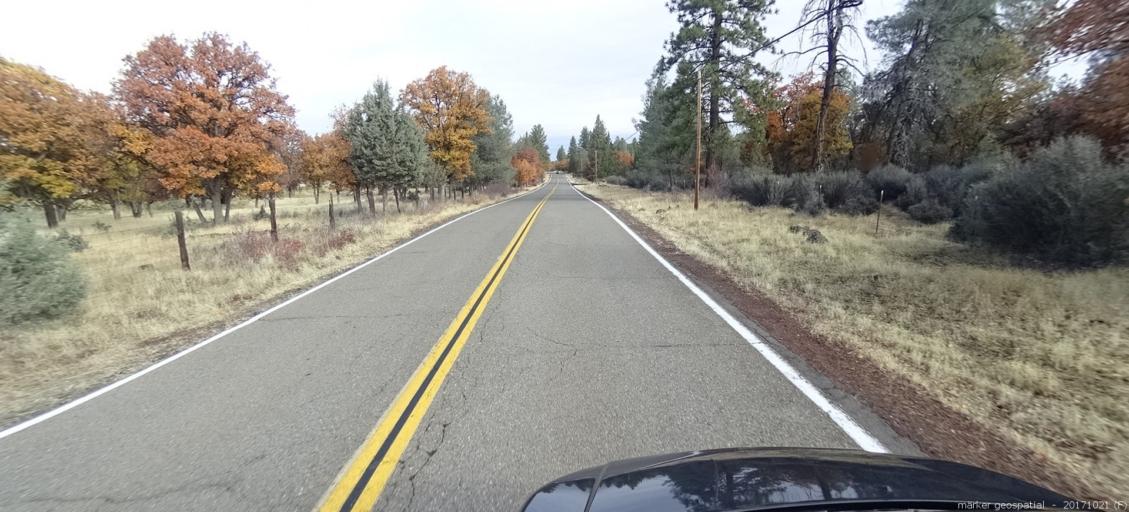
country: US
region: California
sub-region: Shasta County
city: Burney
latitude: 40.9094
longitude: -121.5469
